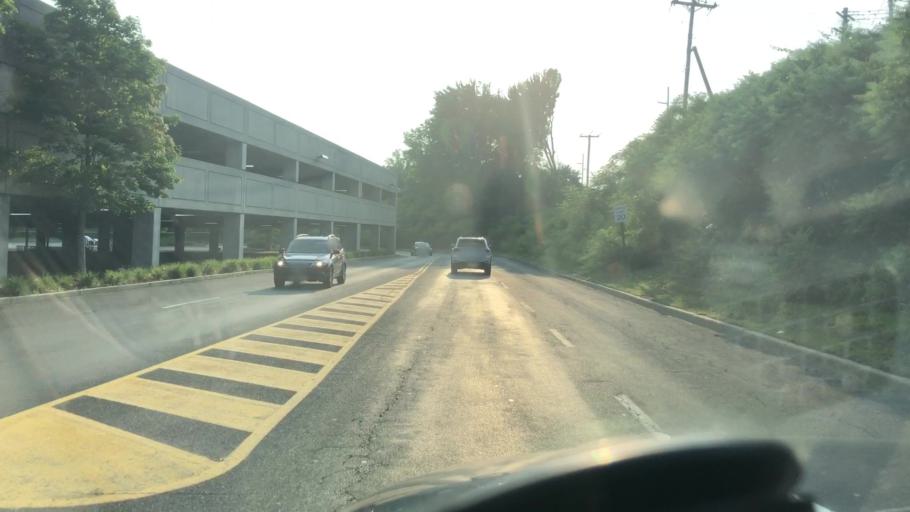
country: US
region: Massachusetts
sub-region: Hampden County
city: Chicopee
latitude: 42.1710
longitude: -72.6415
